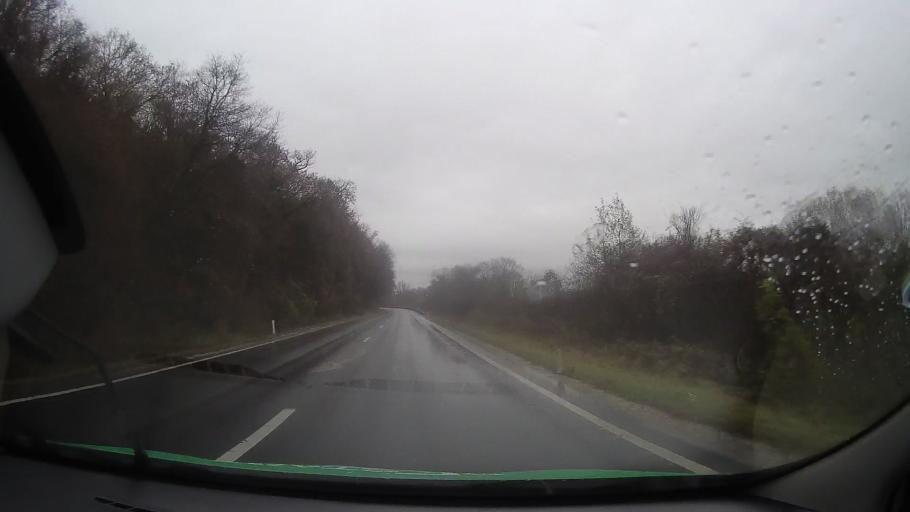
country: RO
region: Mures
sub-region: Comuna Brancovenesti
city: Brancovenesti
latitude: 46.8686
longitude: 24.7702
